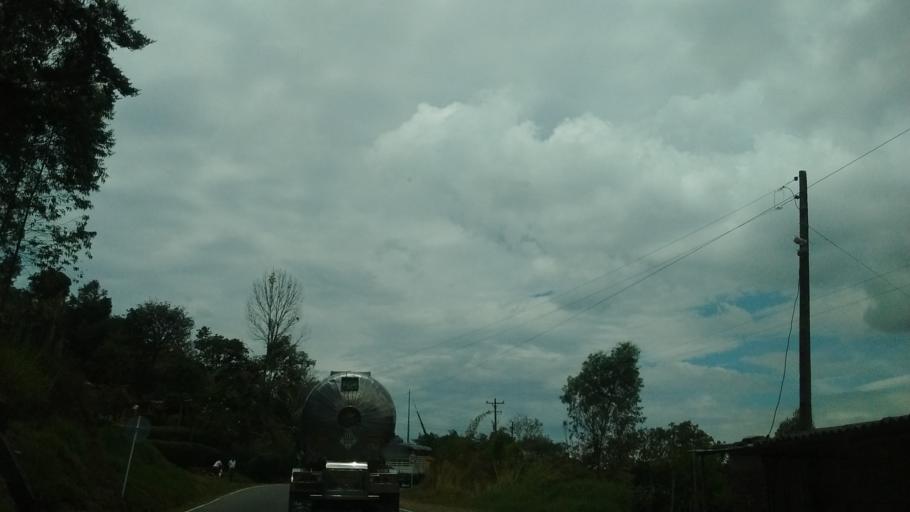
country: CO
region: Cauca
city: Rosas
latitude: 2.3073
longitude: -76.7001
